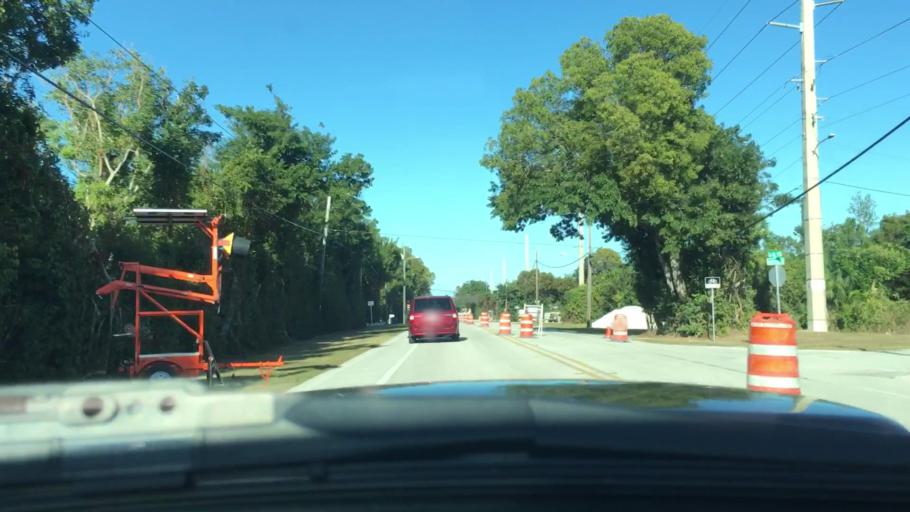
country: US
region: Florida
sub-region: Monroe County
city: North Key Largo
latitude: 25.1906
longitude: -80.3570
